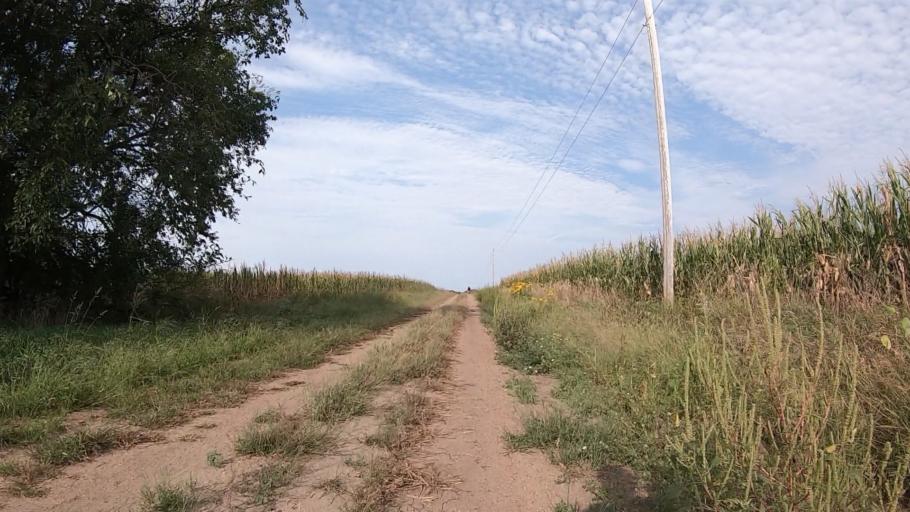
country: US
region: Kansas
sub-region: Washington County
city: Washington
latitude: 39.6750
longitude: -96.9518
